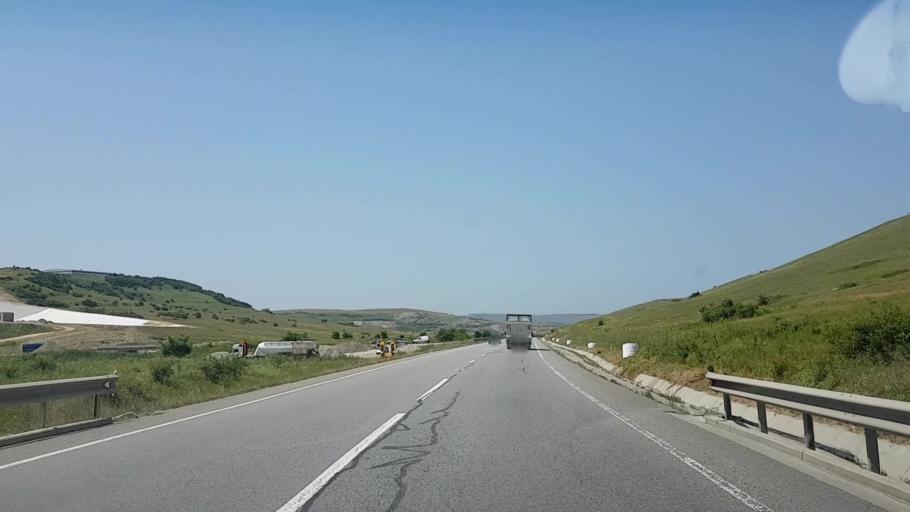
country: RO
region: Cluj
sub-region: Comuna Apahida
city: Dezmir
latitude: 46.7486
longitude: 23.7074
